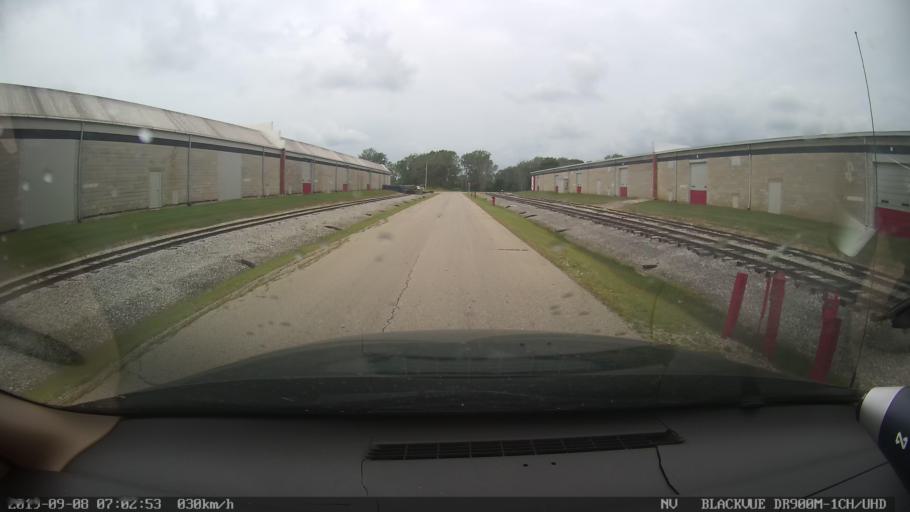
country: US
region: Ohio
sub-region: Richland County
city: Shelby
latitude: 40.8987
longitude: -82.6743
